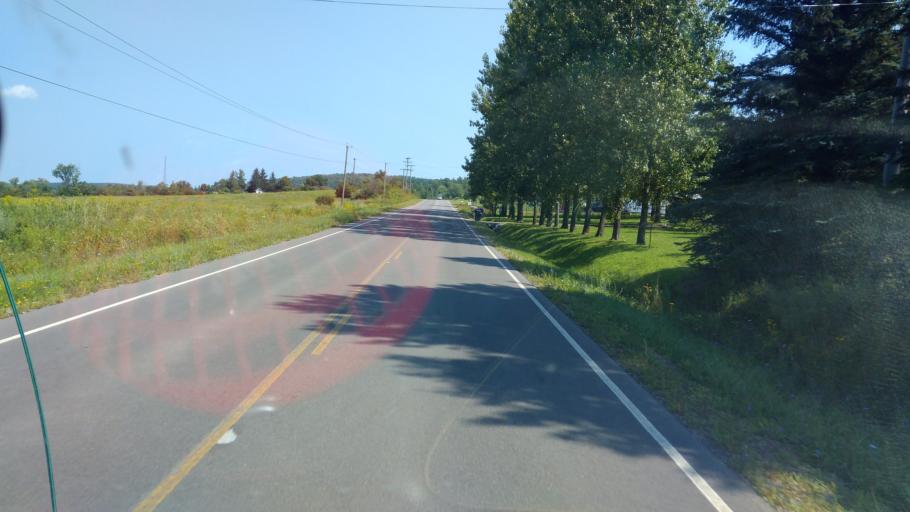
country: US
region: New York
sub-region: Allegany County
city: Belmont
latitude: 42.2812
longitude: -78.0321
